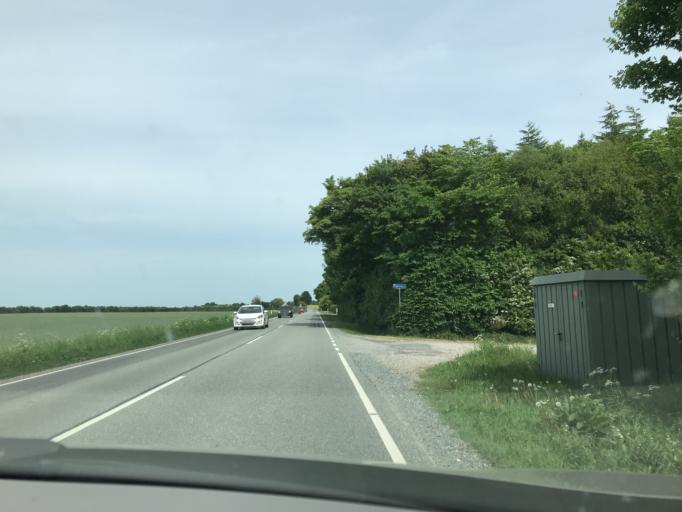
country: DK
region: Central Jutland
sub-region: Norddjurs Kommune
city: Allingabro
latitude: 56.4490
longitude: 10.2880
